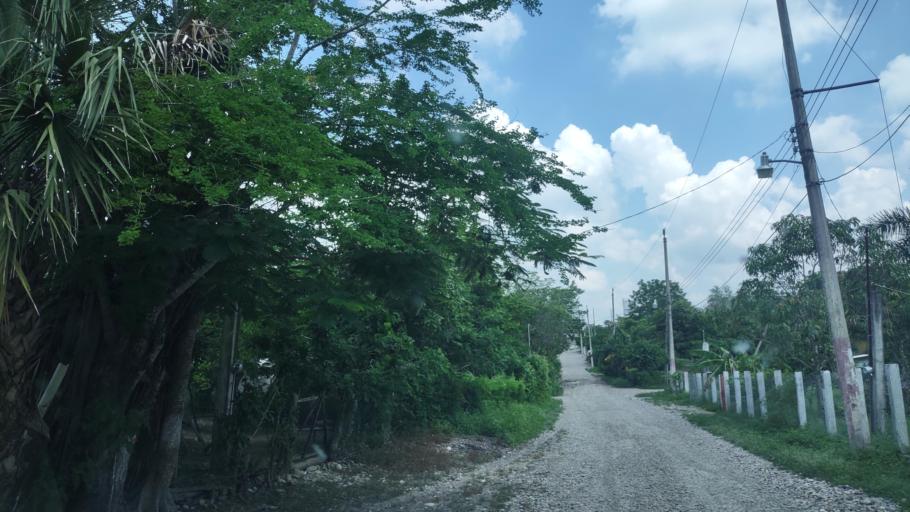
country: MX
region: Veracruz
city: Tempoal de Sanchez
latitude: 21.5461
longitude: -98.2762
